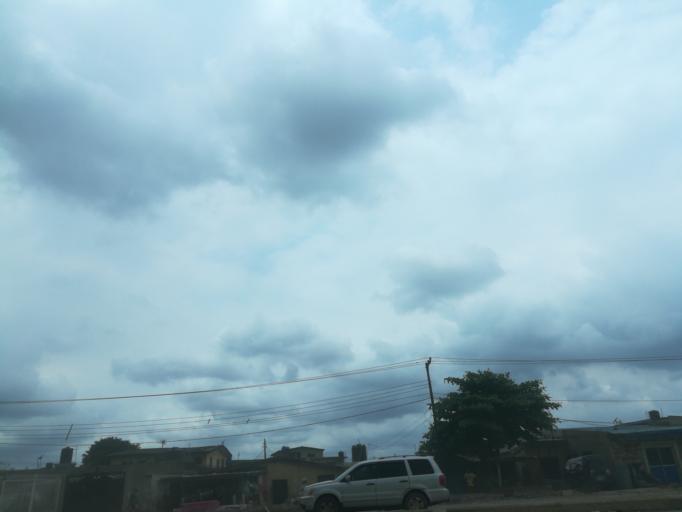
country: NG
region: Lagos
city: Oshodi
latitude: 6.5664
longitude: 3.3475
